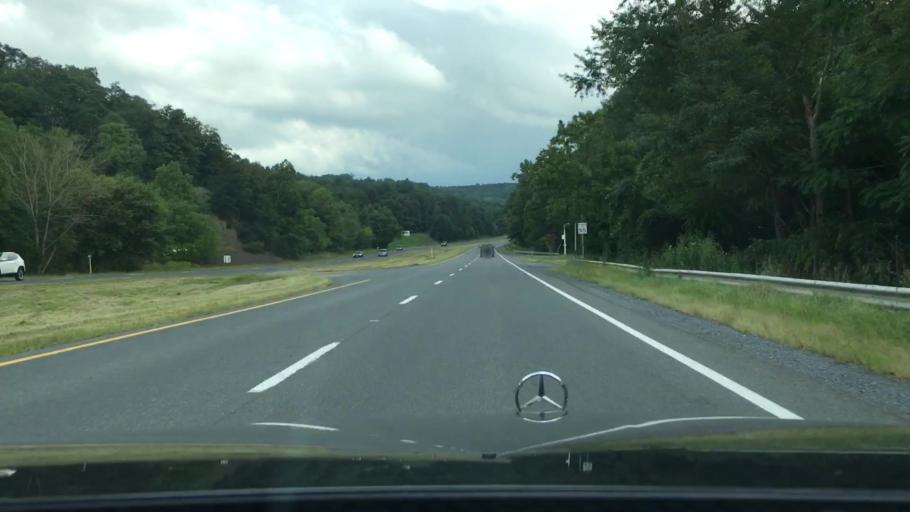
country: US
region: Virginia
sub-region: City of Winchester
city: Winchester
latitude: 39.2668
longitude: -78.2391
